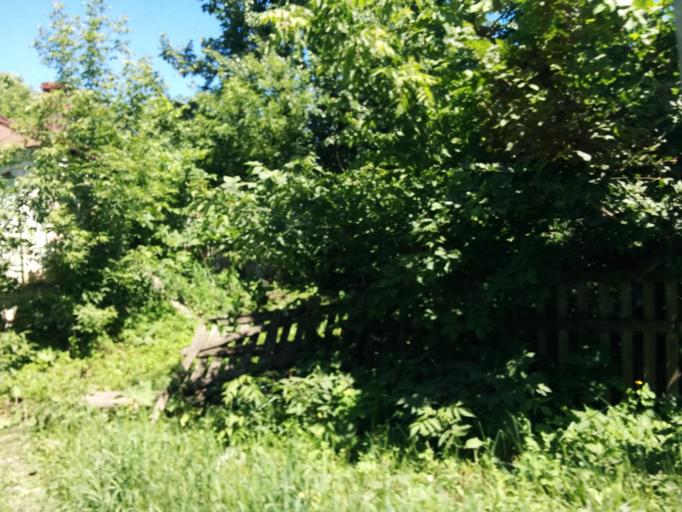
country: RU
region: Tambov
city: Morshansk
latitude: 53.6213
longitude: 41.8507
